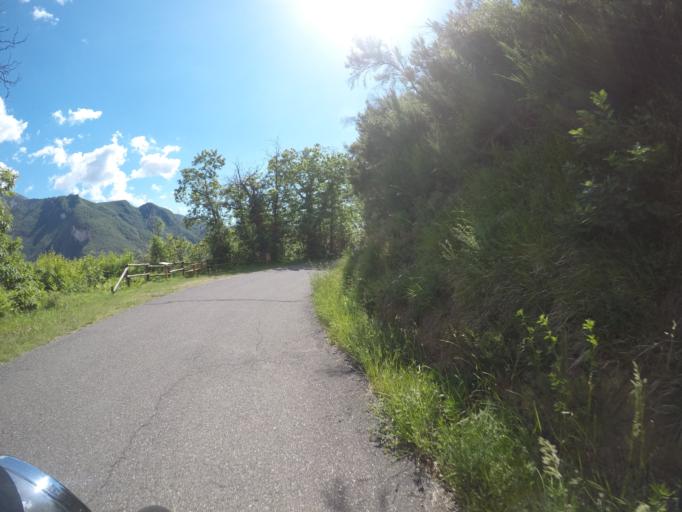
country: IT
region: Tuscany
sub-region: Provincia di Massa-Carrara
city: Casola in Lunigiana
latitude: 44.1762
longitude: 10.1568
